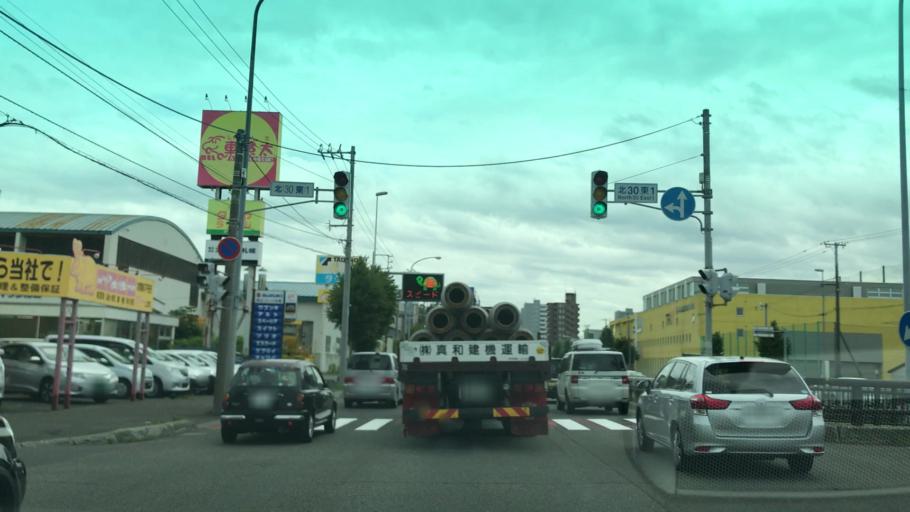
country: JP
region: Hokkaido
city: Sapporo
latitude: 43.0980
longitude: 141.3459
